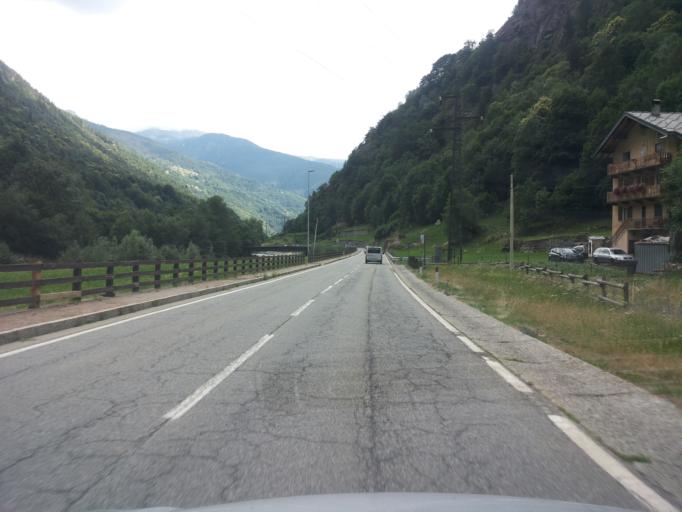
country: IT
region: Aosta Valley
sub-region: Valle d'Aosta
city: Issime
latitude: 45.6742
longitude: 7.8567
